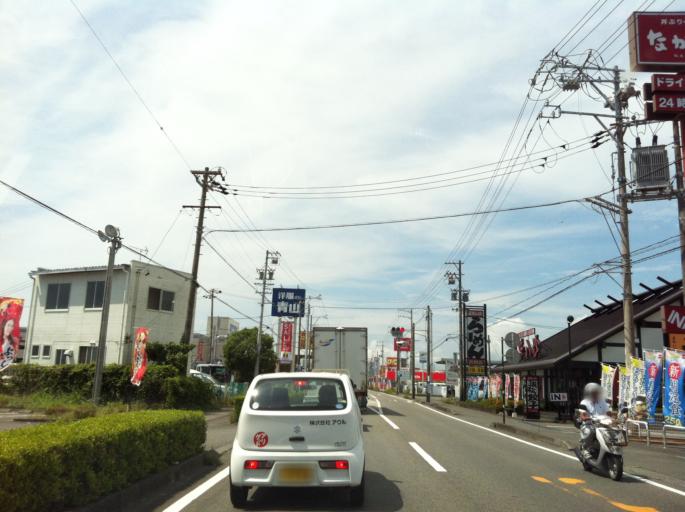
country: JP
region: Shizuoka
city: Shimada
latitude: 34.7627
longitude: 138.2471
